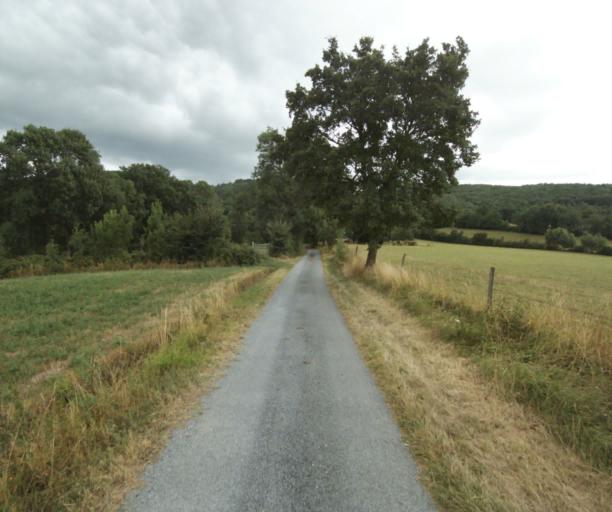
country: FR
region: Midi-Pyrenees
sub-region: Departement du Tarn
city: Soreze
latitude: 43.4609
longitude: 2.0890
